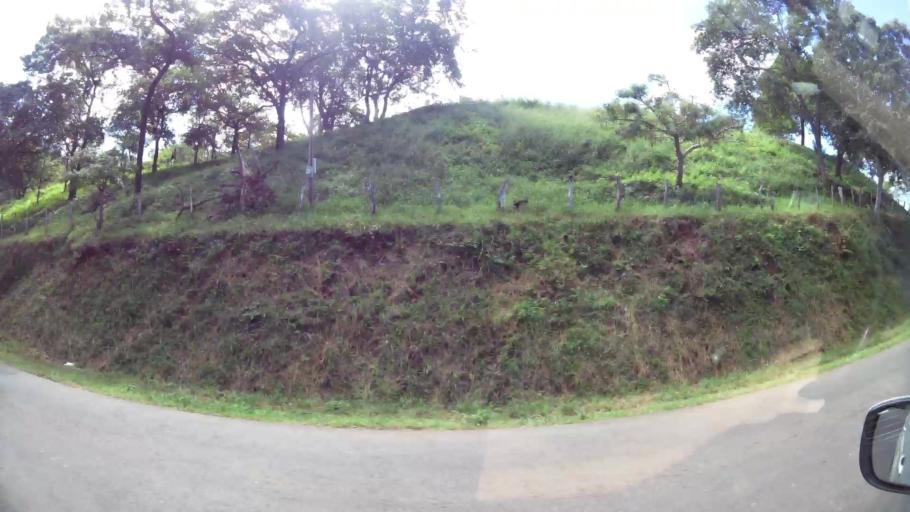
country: CR
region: Guanacaste
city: Santa Cruz
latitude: 10.3107
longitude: -85.8203
